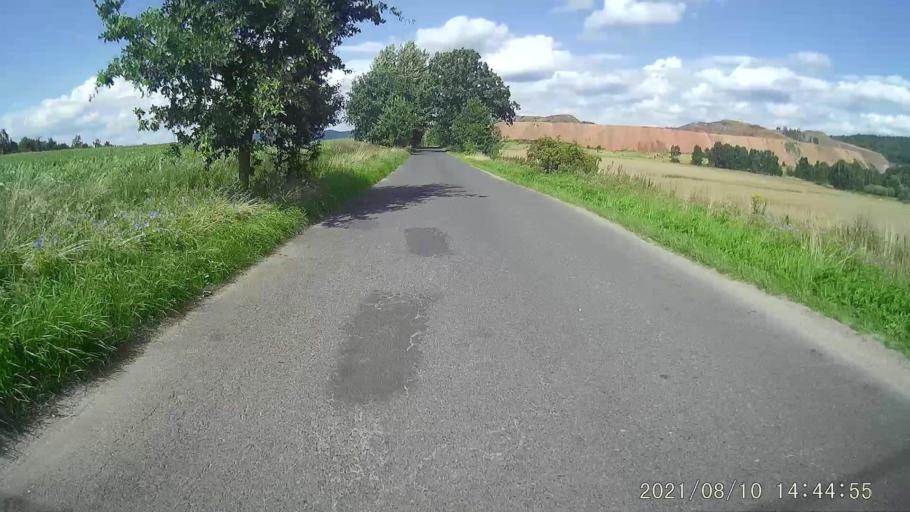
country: PL
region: Lower Silesian Voivodeship
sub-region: Powiat klodzki
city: Radkow
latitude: 50.5371
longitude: 16.4217
